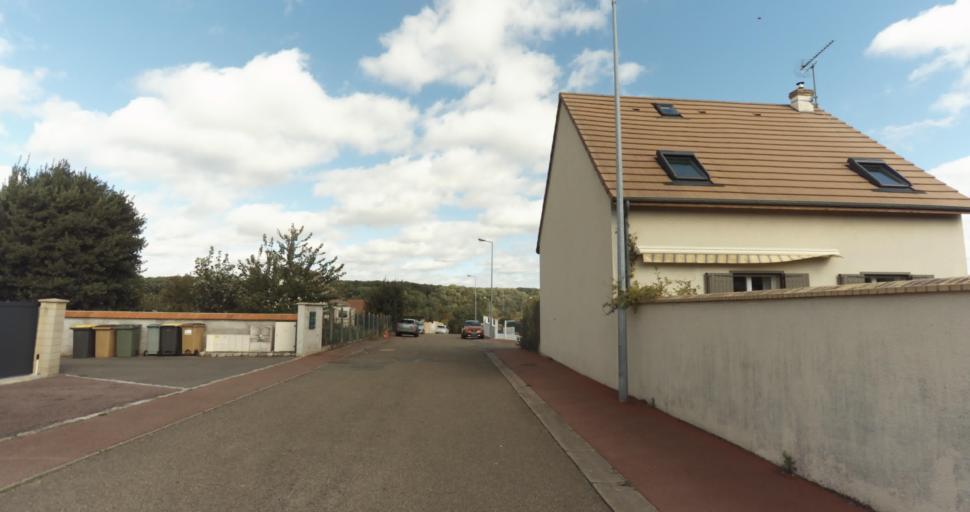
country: FR
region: Centre
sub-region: Departement d'Eure-et-Loir
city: Garnay
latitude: 48.7171
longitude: 1.3365
